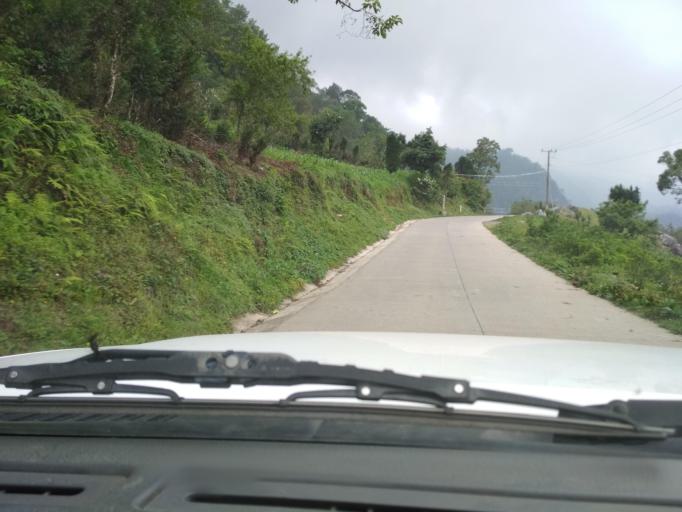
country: MX
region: Veracruz
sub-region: La Perla
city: Metlac Hernandez (Metlac Primero)
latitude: 18.9782
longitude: -97.1374
